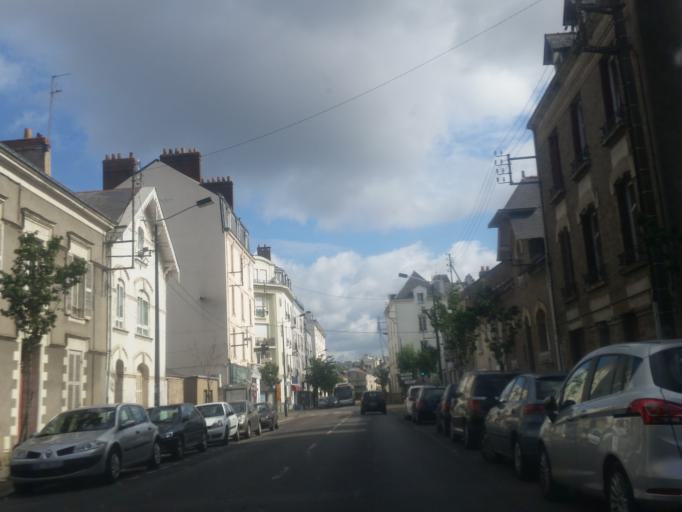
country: FR
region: Pays de la Loire
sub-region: Departement de la Loire-Atlantique
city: Nantes
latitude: 47.2244
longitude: -1.5297
